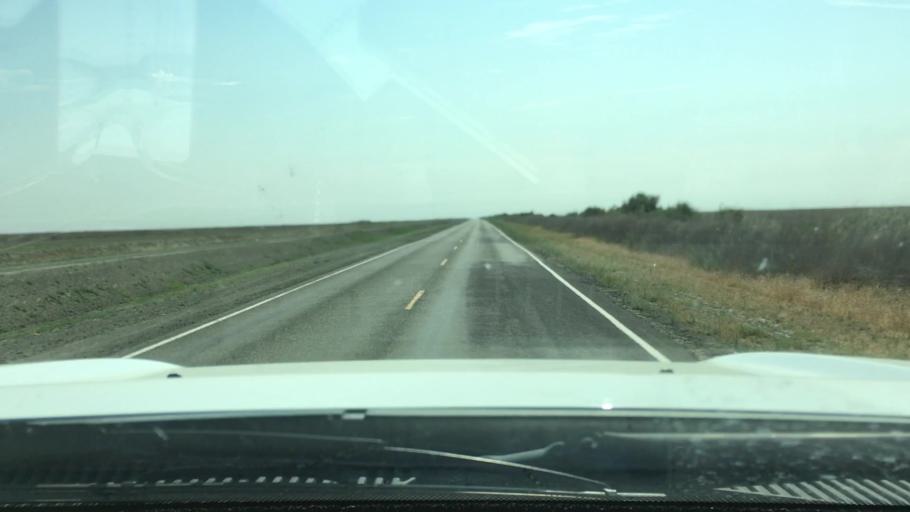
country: US
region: California
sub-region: Kings County
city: Kettleman City
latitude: 35.9340
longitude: -119.7393
